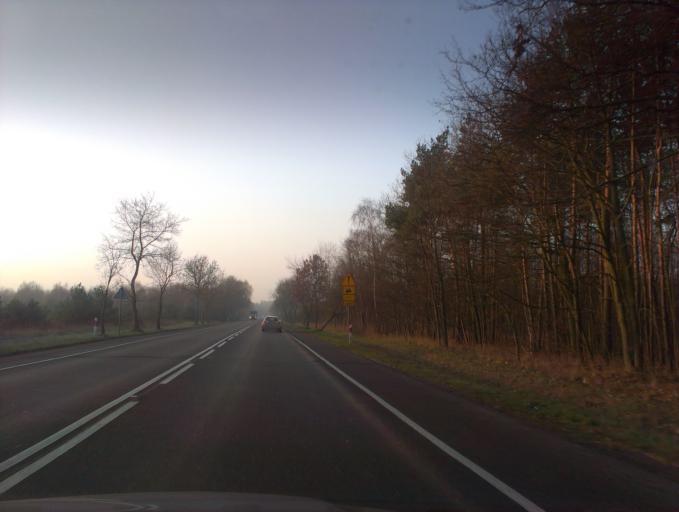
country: PL
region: Greater Poland Voivodeship
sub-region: Powiat obornicki
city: Rogozno
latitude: 52.7315
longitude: 16.9405
